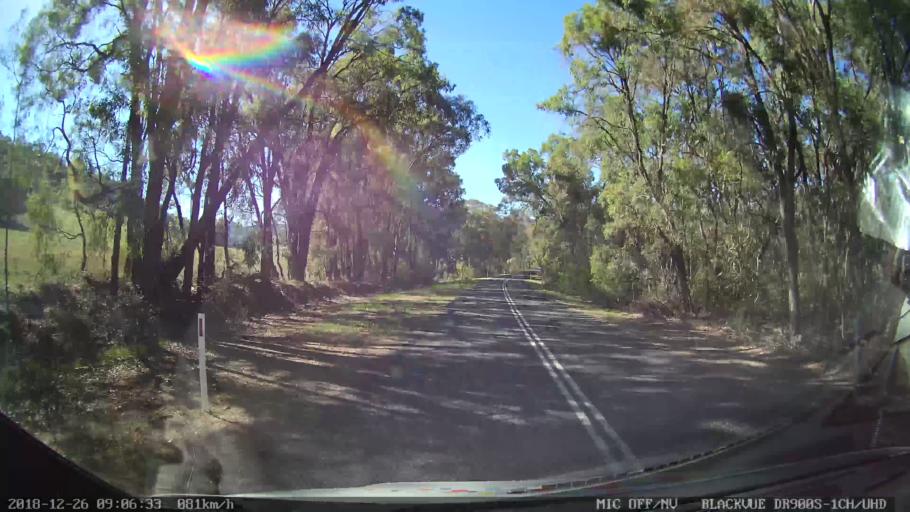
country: AU
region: New South Wales
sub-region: Mid-Western Regional
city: Kandos
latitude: -32.6954
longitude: 150.0058
